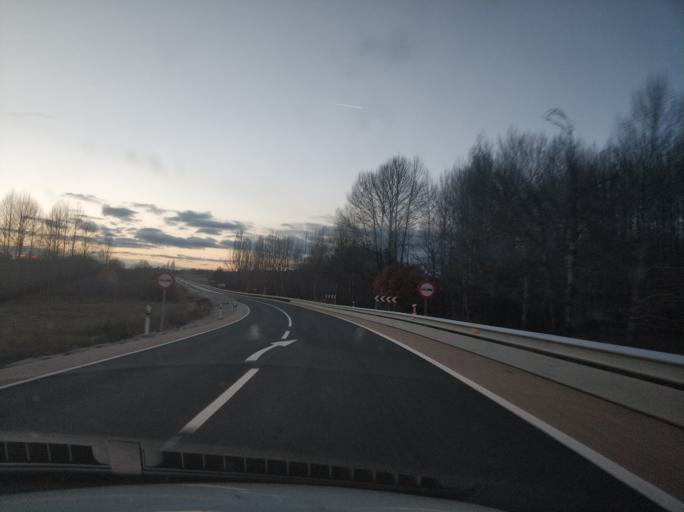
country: ES
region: Castille and Leon
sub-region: Provincia de Soria
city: Cidones
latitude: 41.8133
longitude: -2.7090
